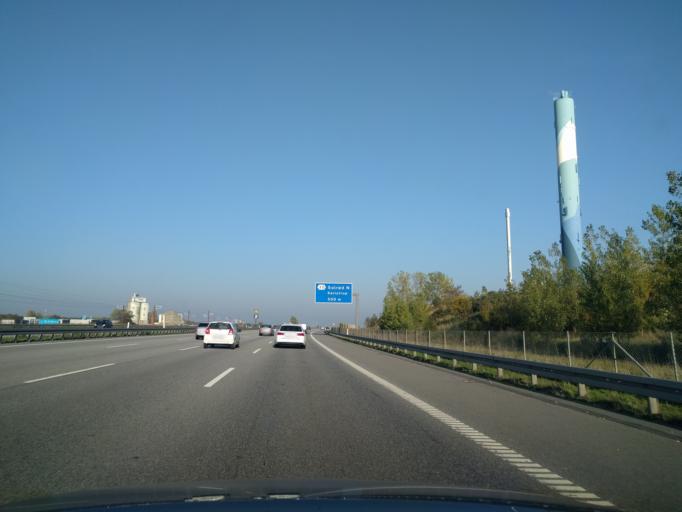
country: DK
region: Zealand
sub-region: Solrod Kommune
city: Solrod Strand
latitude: 55.5399
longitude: 12.2056
